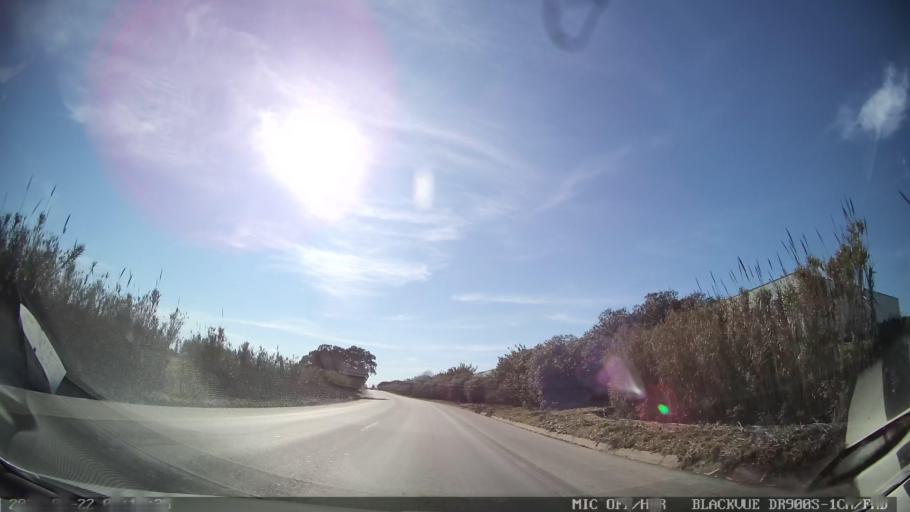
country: PT
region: Lisbon
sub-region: Alenquer
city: Carregado
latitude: 39.0422
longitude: -8.9264
